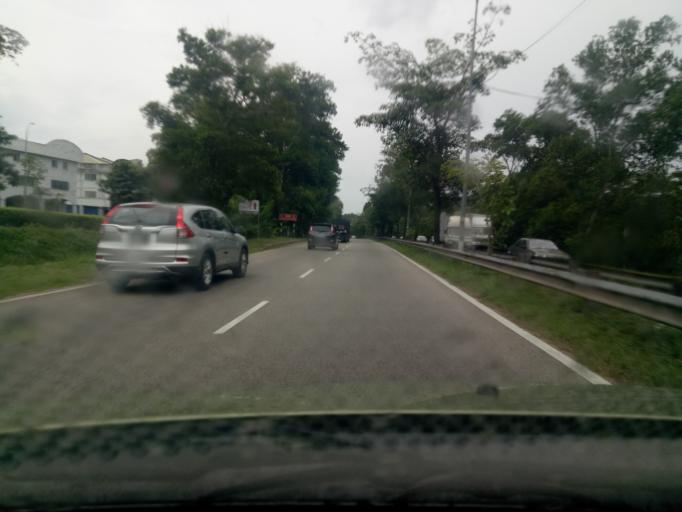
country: MY
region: Kedah
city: Sungai Petani
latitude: 5.6690
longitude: 100.5083
